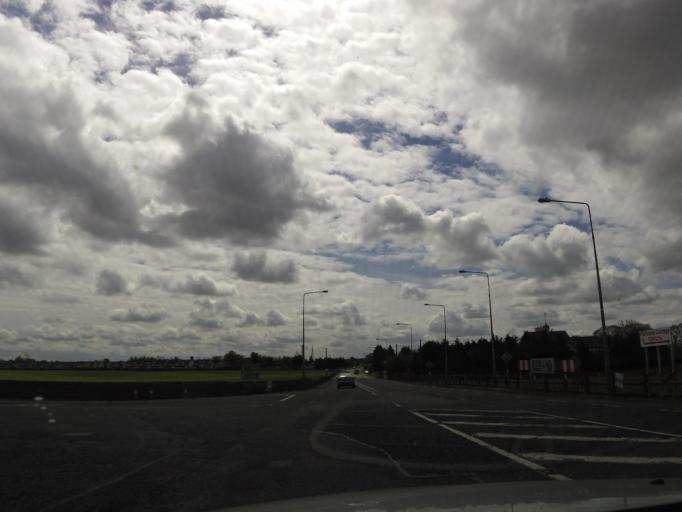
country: IE
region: Connaught
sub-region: County Galway
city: Tuam
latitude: 53.5301
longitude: -8.8488
